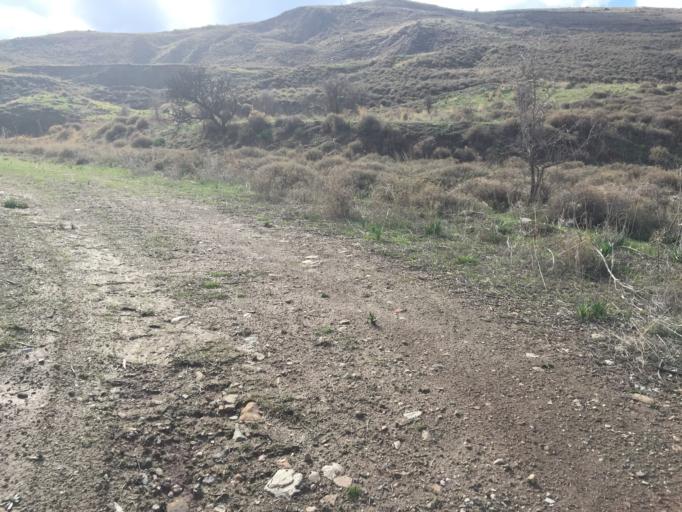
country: CY
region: Limassol
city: Pachna
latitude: 34.8724
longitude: 32.6601
